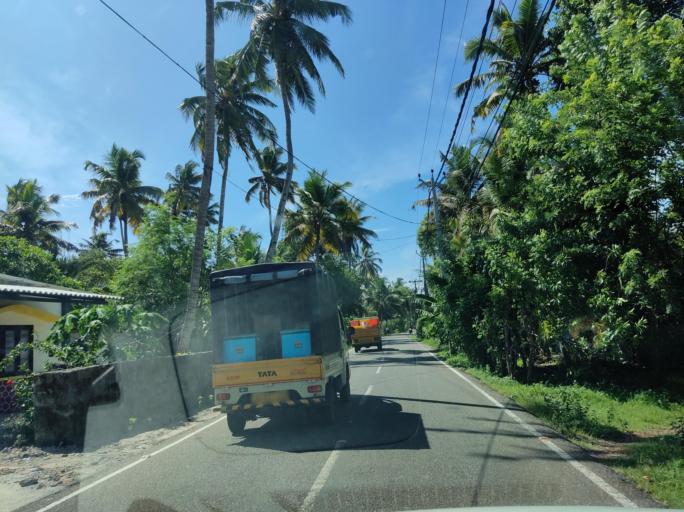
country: IN
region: Kerala
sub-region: Alappuzha
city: Kayankulam
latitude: 9.1760
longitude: 76.4455
